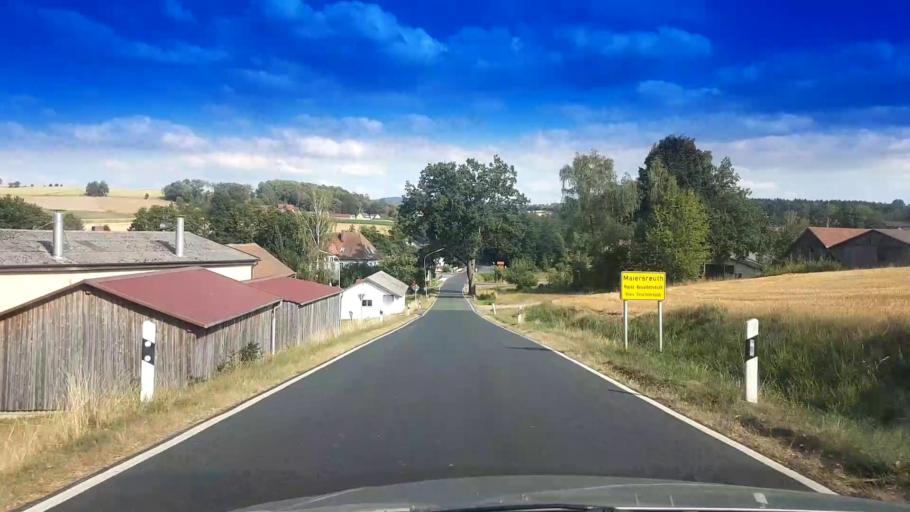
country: DE
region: Bavaria
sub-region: Upper Palatinate
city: Neualbenreuth
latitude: 49.9893
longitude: 12.4064
